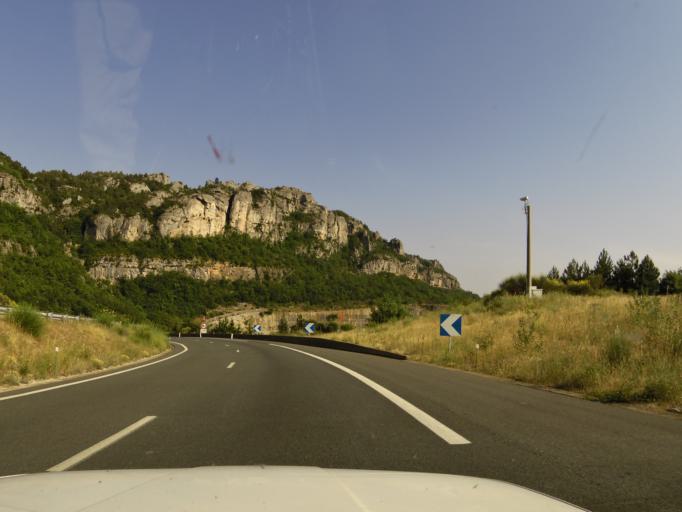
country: FR
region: Languedoc-Roussillon
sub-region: Departement de l'Herault
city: Lodeve
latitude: 43.8248
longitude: 3.3171
